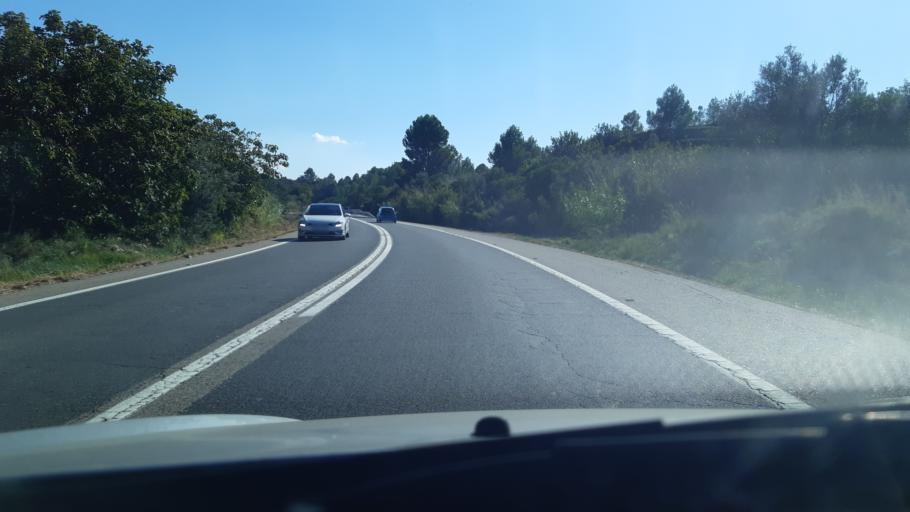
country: ES
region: Catalonia
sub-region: Provincia de Tarragona
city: Tivenys
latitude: 40.9016
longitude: 0.4829
